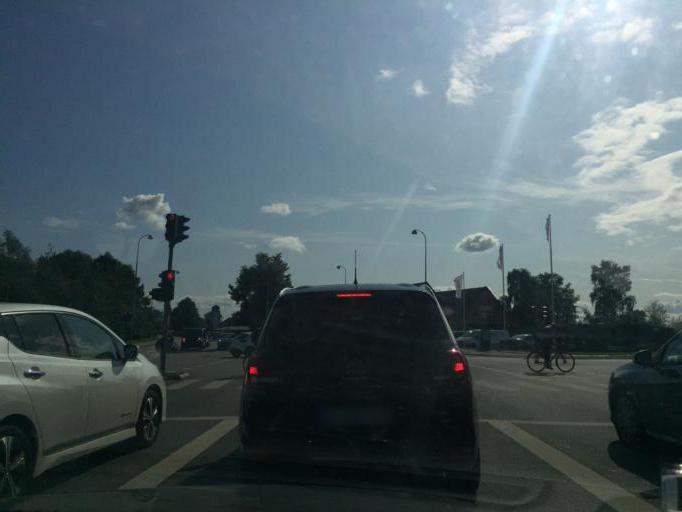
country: DK
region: Capital Region
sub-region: Herlev Kommune
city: Herlev
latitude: 55.7270
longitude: 12.4732
